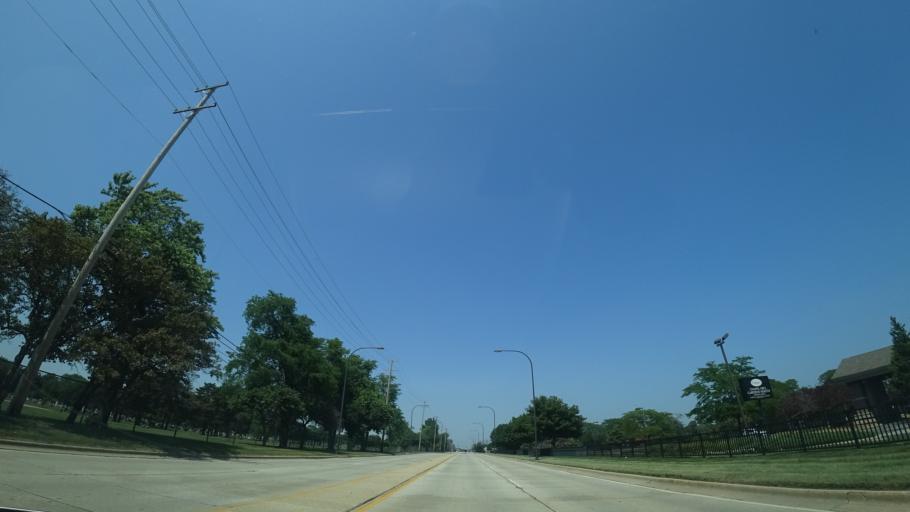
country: US
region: Illinois
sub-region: Cook County
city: Oak Lawn
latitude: 41.6857
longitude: -87.7590
